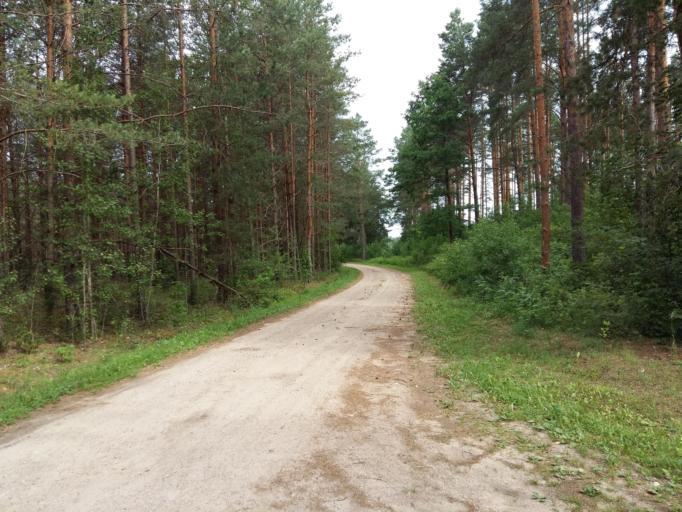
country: LT
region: Alytaus apskritis
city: Druskininkai
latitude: 54.1523
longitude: 24.1350
